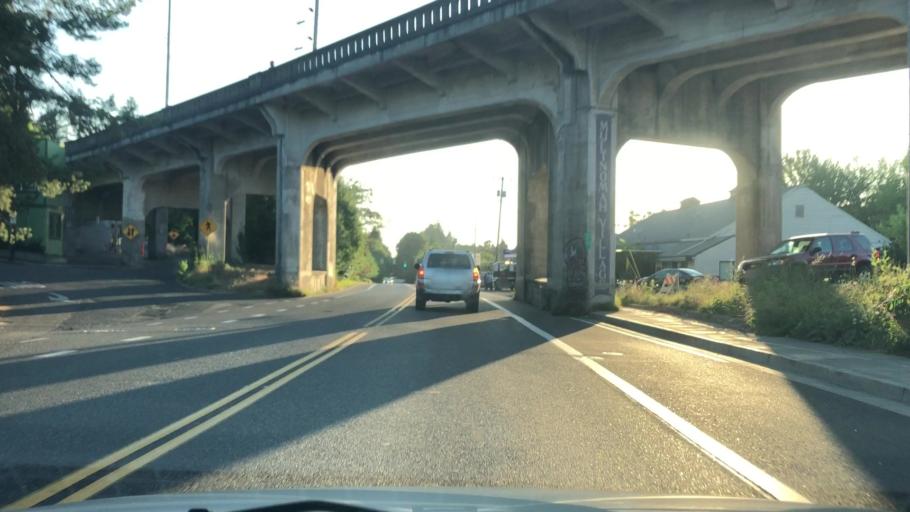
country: US
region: Oregon
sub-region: Washington County
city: Garden Home-Whitford
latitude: 45.4726
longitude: -122.7215
